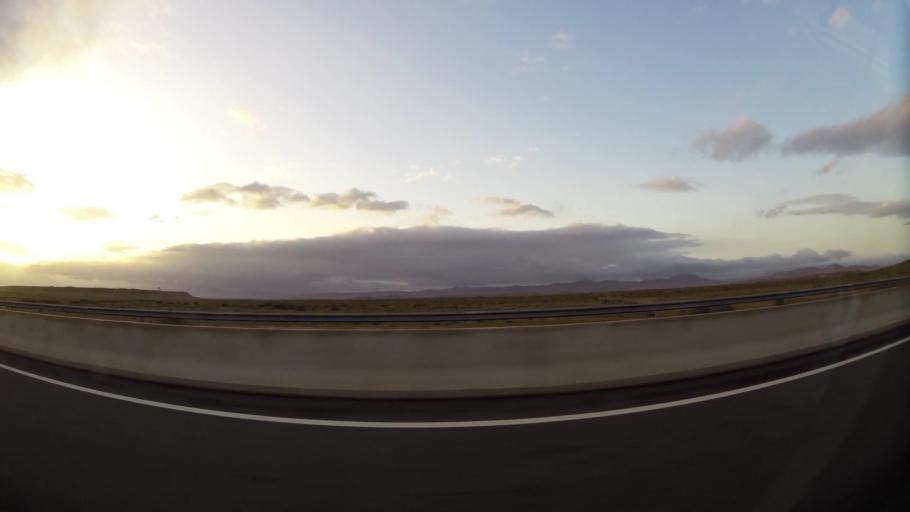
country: MA
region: Oriental
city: Taourirt
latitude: 34.5493
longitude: -2.8819
